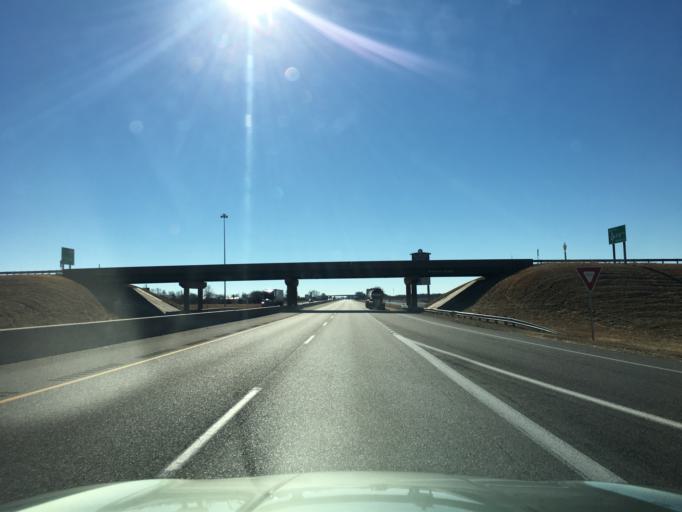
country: US
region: Kansas
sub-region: Sumner County
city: Mulvane
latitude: 37.4730
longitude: -97.3229
